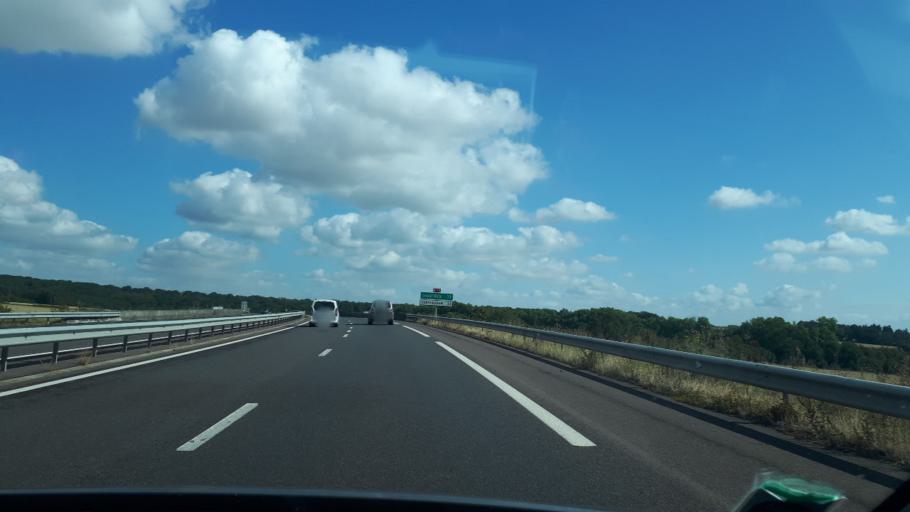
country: FR
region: Centre
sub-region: Departement du Loir-et-Cher
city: Saint-Ouen
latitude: 47.8498
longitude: 1.1050
